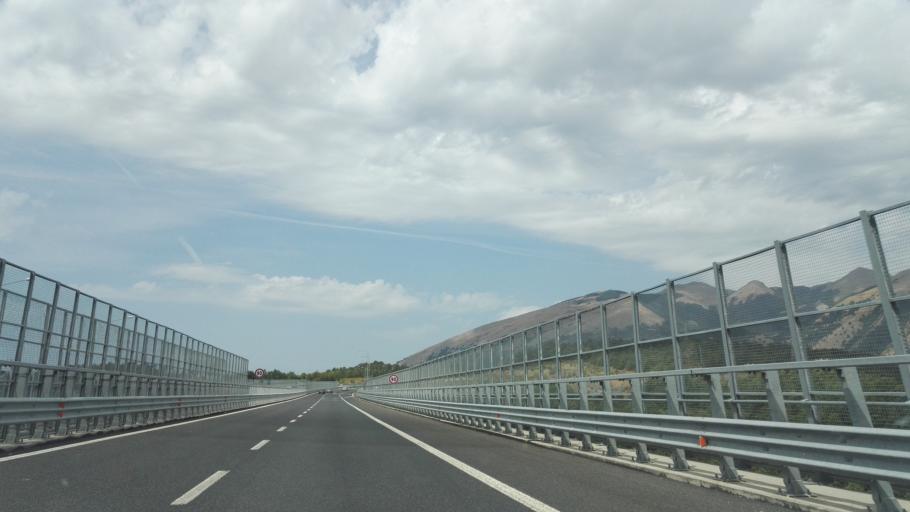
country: IT
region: Basilicate
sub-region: Provincia di Potenza
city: Lauria
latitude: 40.0738
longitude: 15.8620
